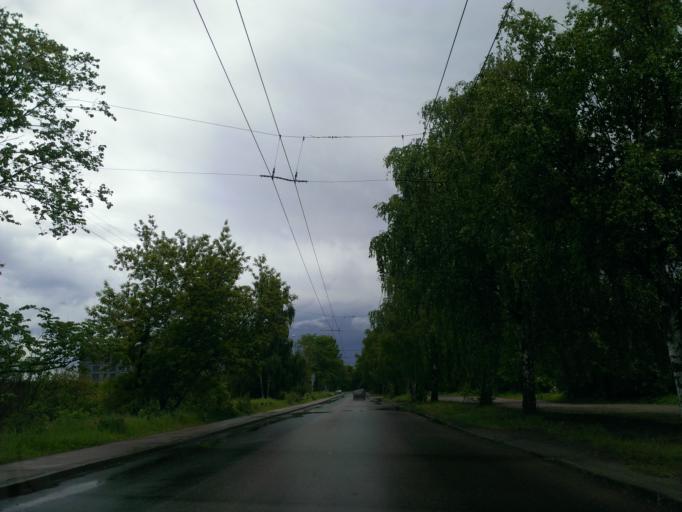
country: LV
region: Riga
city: Riga
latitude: 56.9337
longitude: 24.0953
